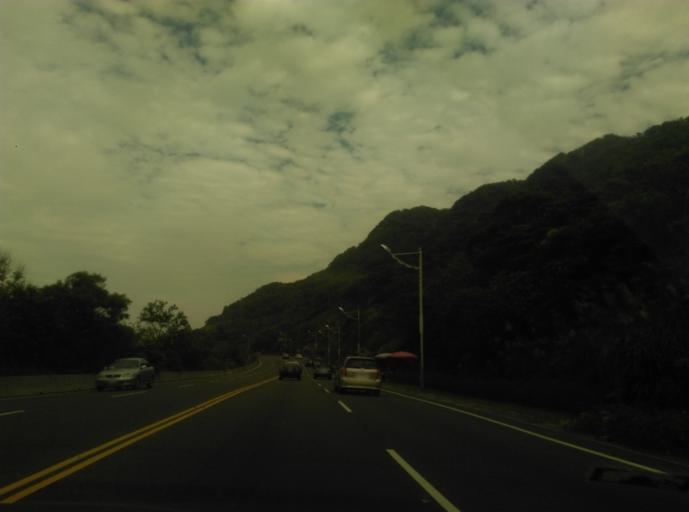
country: TW
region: Taiwan
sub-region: Keelung
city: Keelung
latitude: 25.1601
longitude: 121.6996
